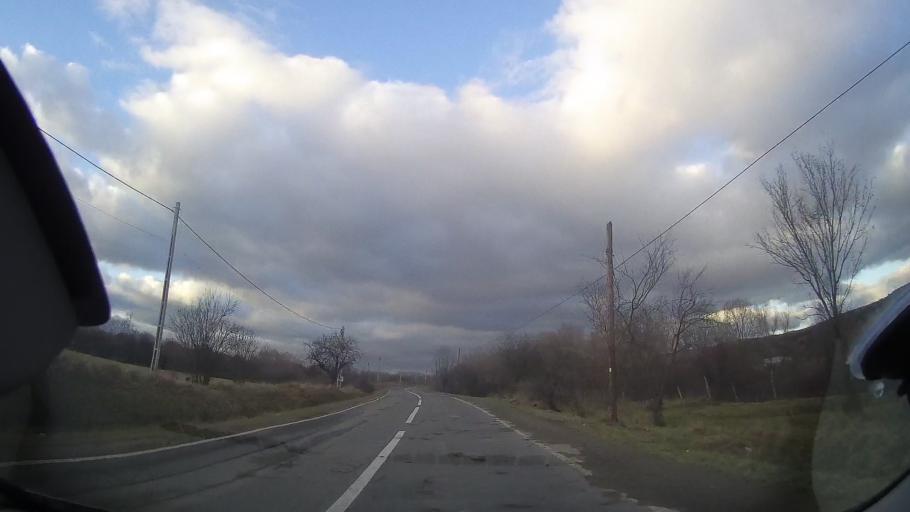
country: RO
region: Cluj
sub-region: Comuna Calatele
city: Calatele
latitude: 46.7799
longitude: 23.0058
